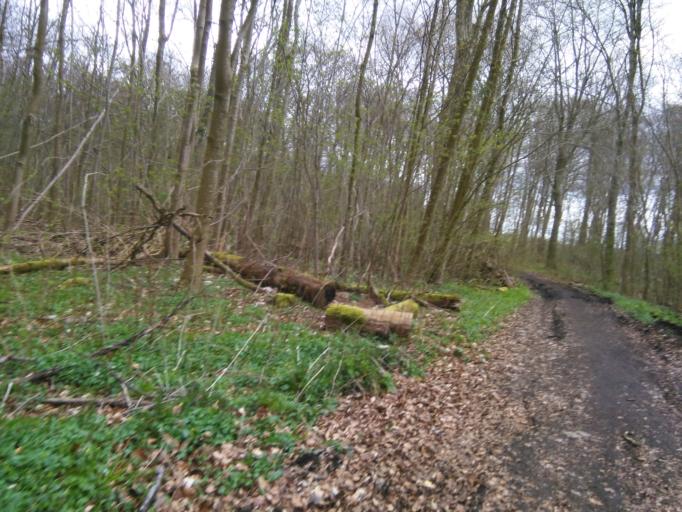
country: DK
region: Central Jutland
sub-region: Favrskov Kommune
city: Soften
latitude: 56.2247
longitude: 10.0759
